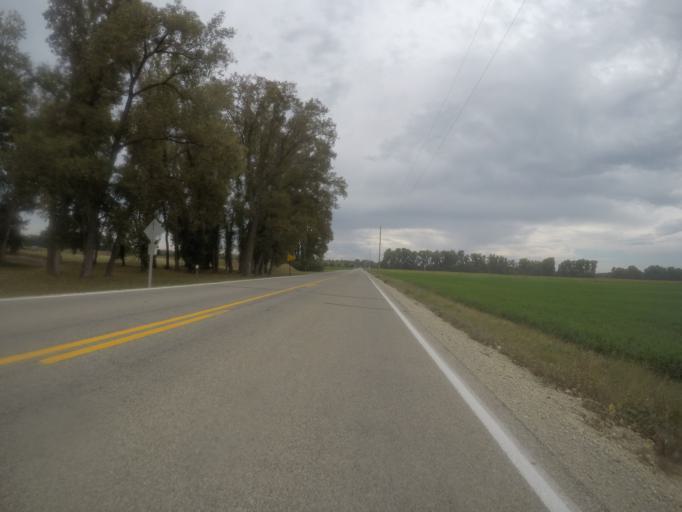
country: US
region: Kansas
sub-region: Riley County
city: Manhattan
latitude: 39.1490
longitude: -96.5887
